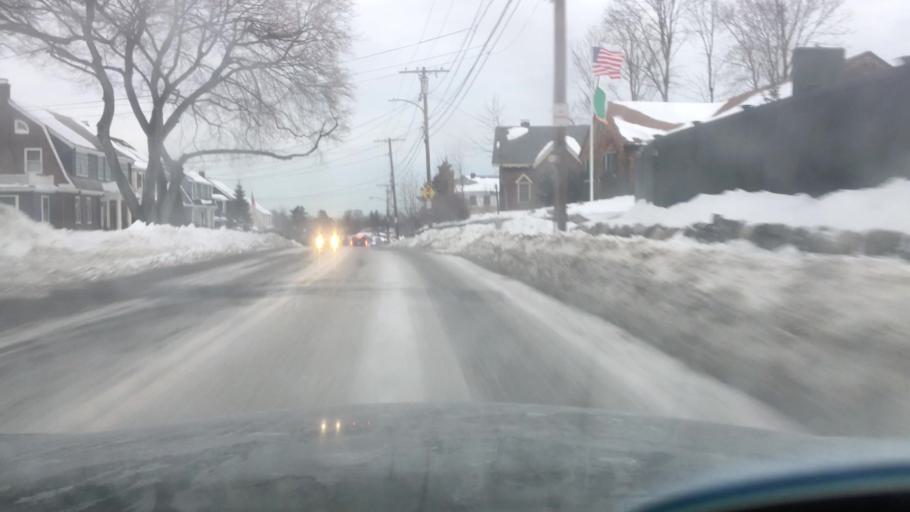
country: US
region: Massachusetts
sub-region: Middlesex County
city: Watertown
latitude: 42.3778
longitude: -71.1762
